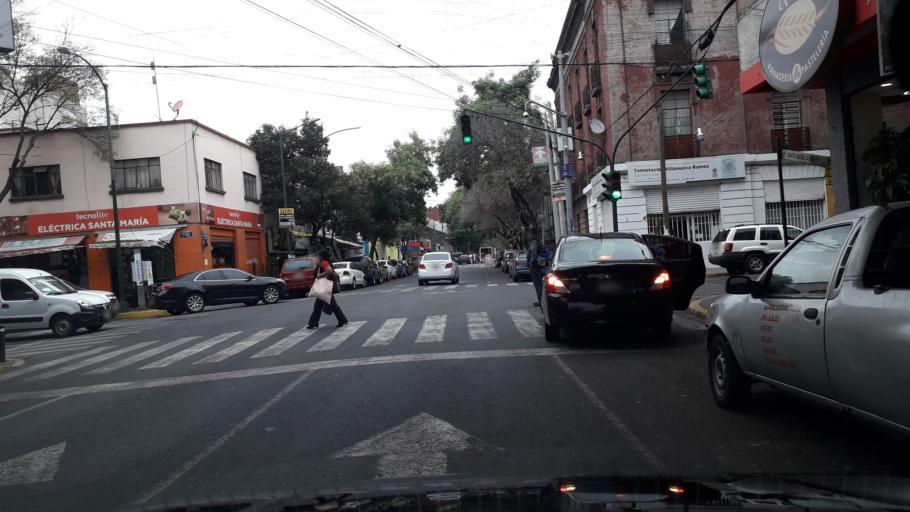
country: MX
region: Mexico City
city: Cuauhtemoc
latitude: 19.4451
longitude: -99.1576
